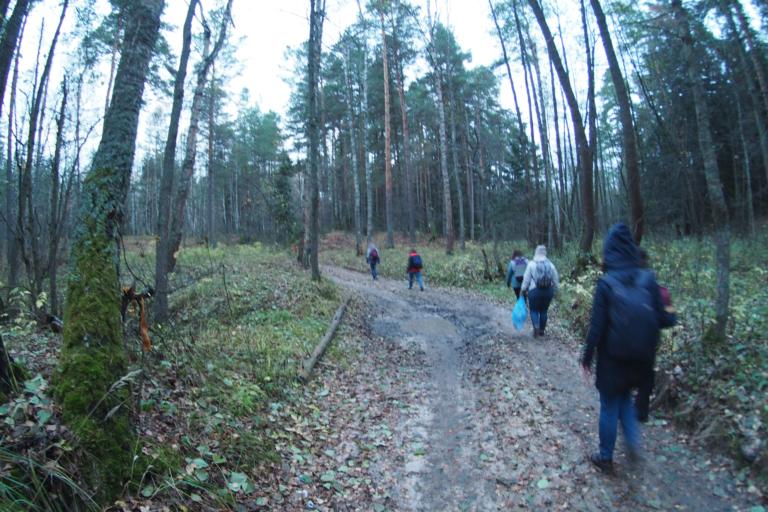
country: RU
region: Moskovskaya
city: Davydovo
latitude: 55.5440
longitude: 38.8423
